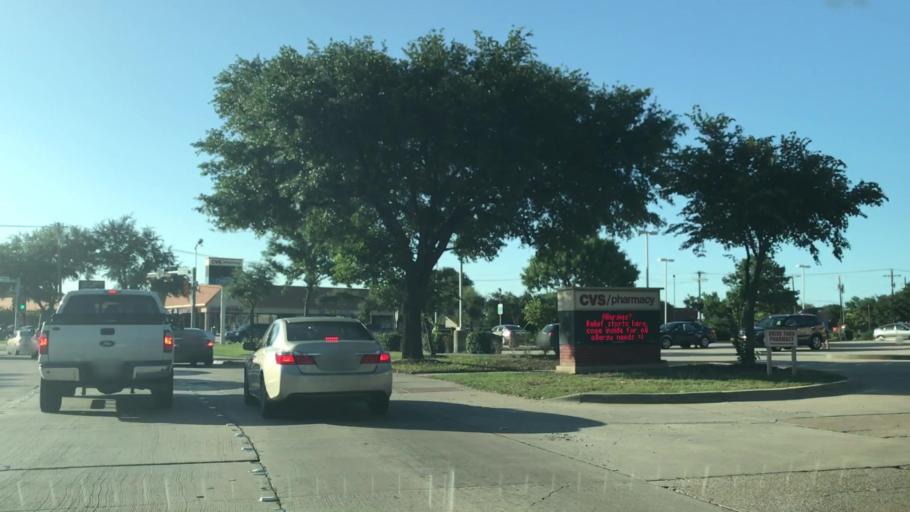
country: US
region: Texas
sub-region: Collin County
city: Plano
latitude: 33.0401
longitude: -96.7078
